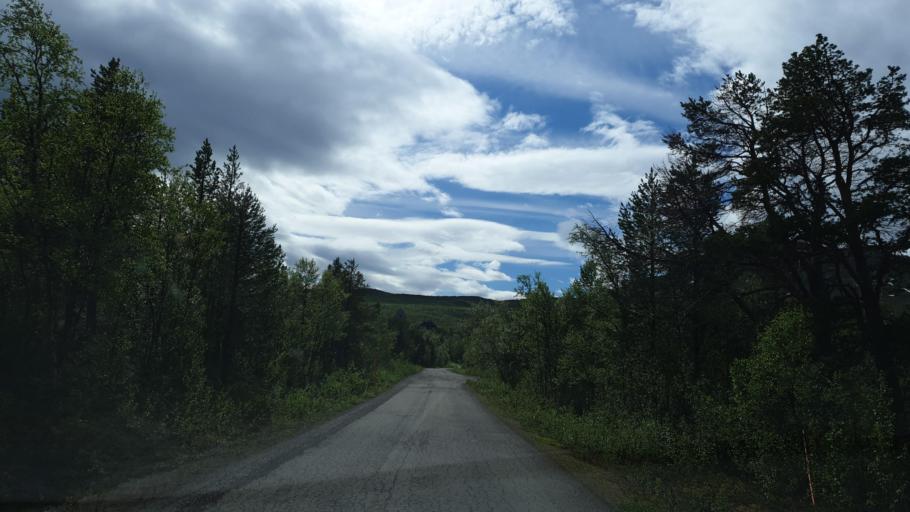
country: SE
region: Norrbotten
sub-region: Kiruna Kommun
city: Kiruna
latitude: 68.2244
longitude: 19.7163
